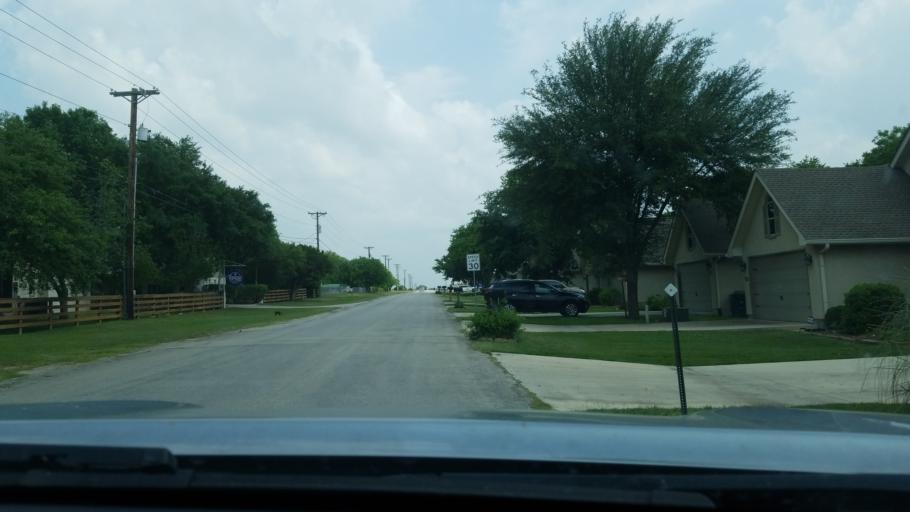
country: US
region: Texas
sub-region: Comal County
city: New Braunfels
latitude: 29.7431
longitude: -98.0993
